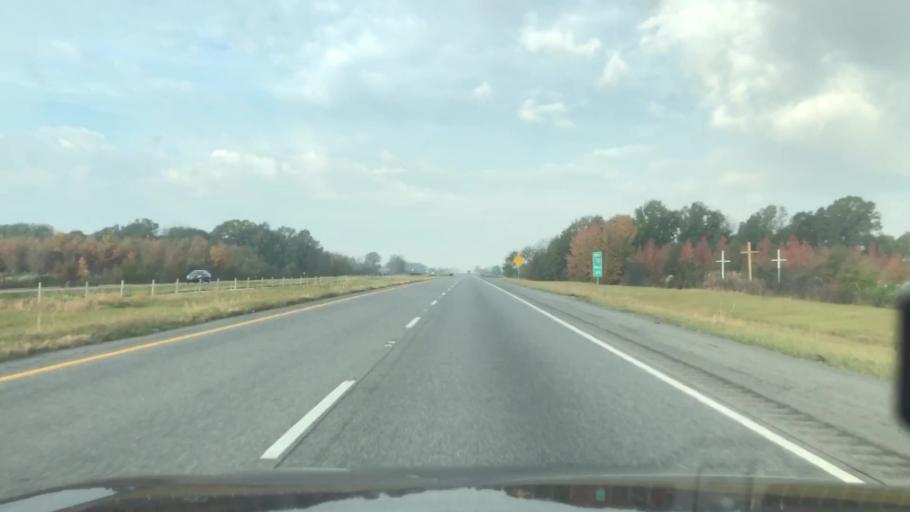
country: US
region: Louisiana
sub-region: Madison Parish
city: Tallulah
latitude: 32.4207
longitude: -91.3166
